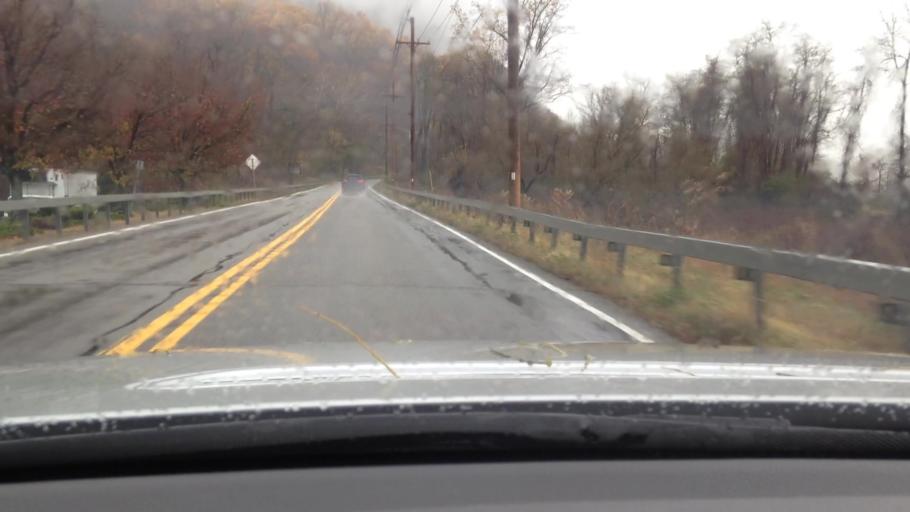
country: US
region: New York
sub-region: Putnam County
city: Cold Spring
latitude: 41.4408
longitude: -73.9749
